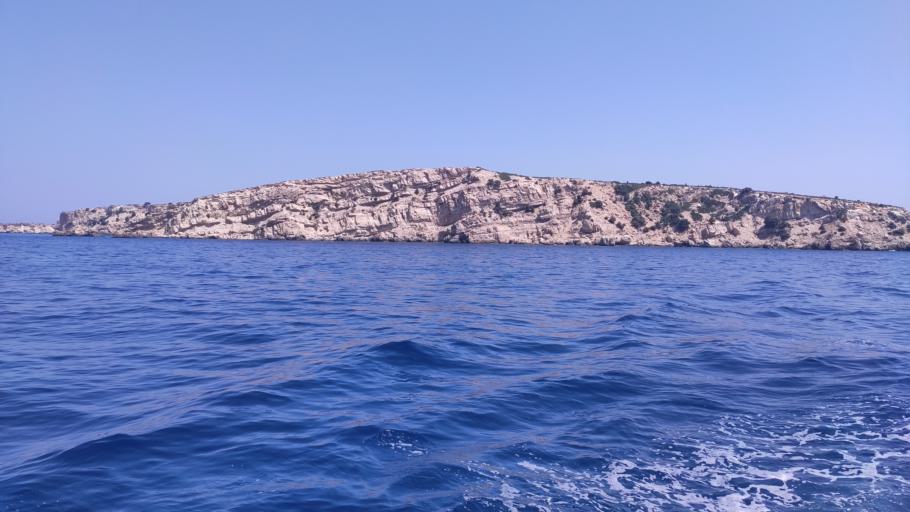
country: GR
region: South Aegean
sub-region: Nomos Dodekanisou
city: Kalymnos
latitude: 36.9332
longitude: 27.0896
